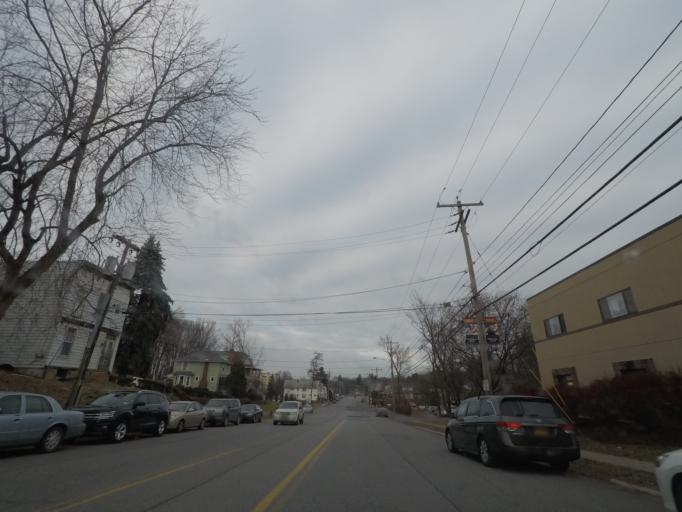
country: US
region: New York
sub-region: Rensselaer County
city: Troy
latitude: 42.7352
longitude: -73.6709
